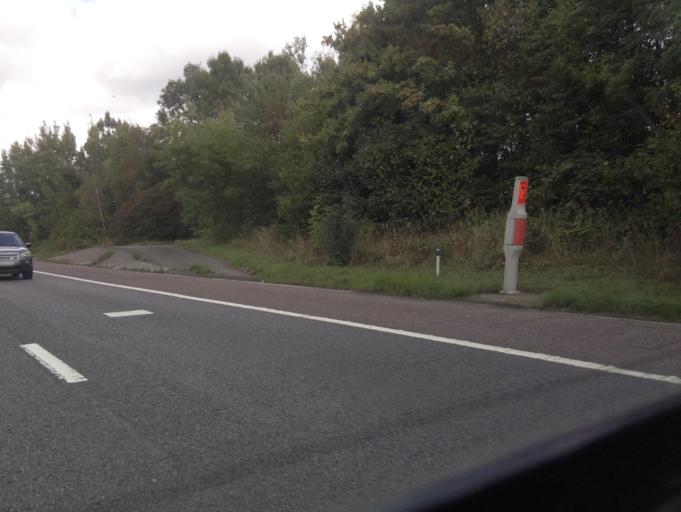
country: GB
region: England
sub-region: Borough of Tameside
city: Denton
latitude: 53.4385
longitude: -2.1301
